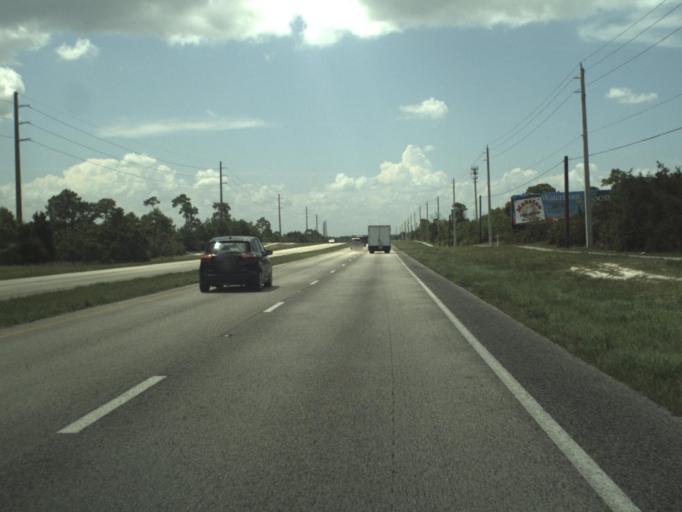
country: US
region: Florida
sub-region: Martin County
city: Hobe Sound
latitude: 27.0924
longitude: -80.1542
